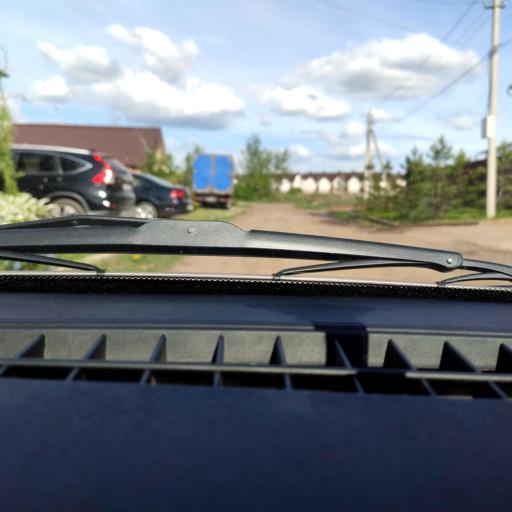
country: RU
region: Bashkortostan
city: Avdon
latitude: 54.6975
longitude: 55.7928
